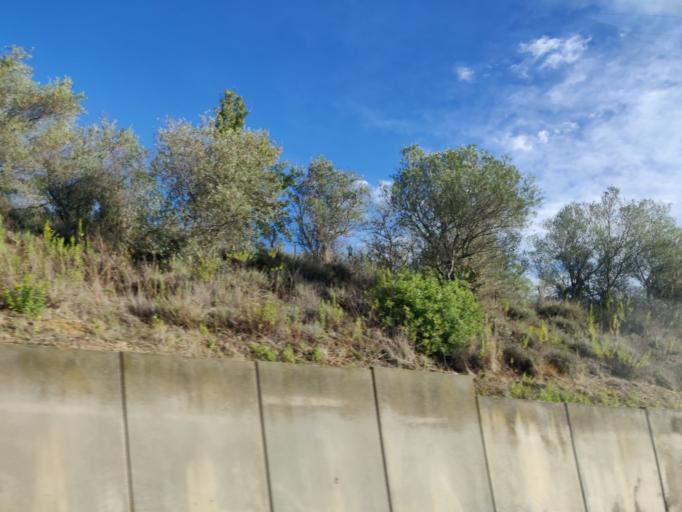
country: IT
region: Tuscany
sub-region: Provincia di Grosseto
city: Gavorrano
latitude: 42.9504
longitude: 10.8877
